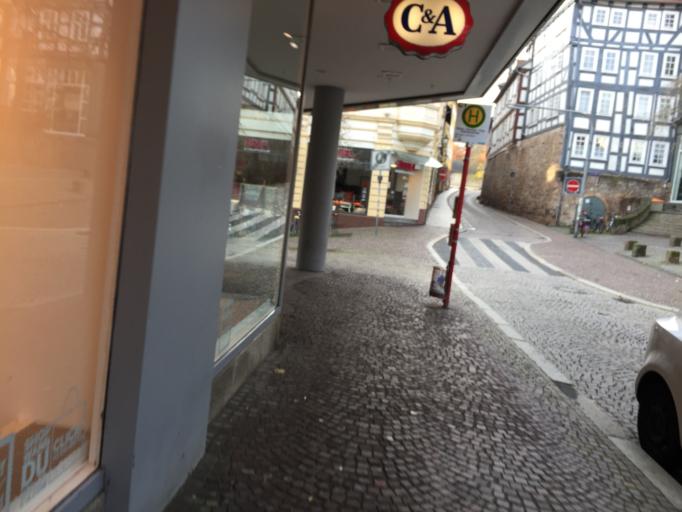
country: DE
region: Hesse
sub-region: Regierungsbezirk Giessen
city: Marburg an der Lahn
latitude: 50.8076
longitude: 8.7688
